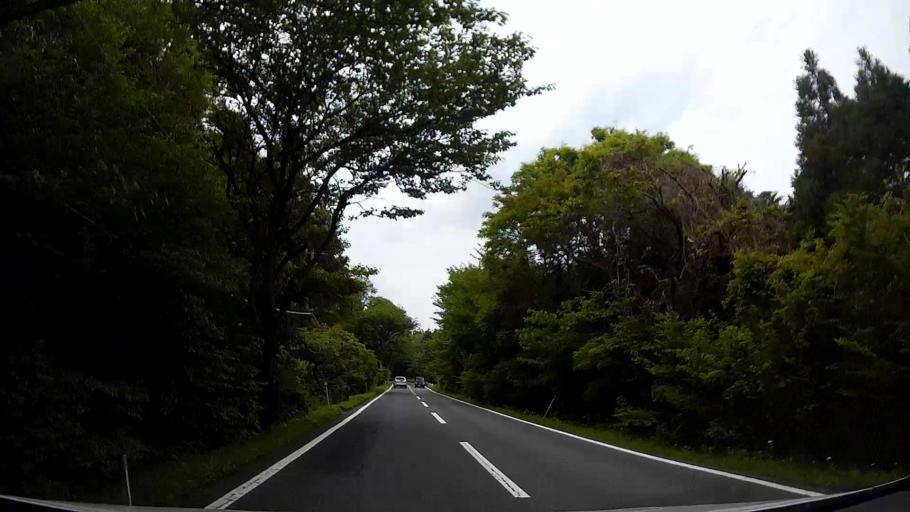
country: JP
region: Shizuoka
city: Ito
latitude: 34.9061
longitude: 139.0852
